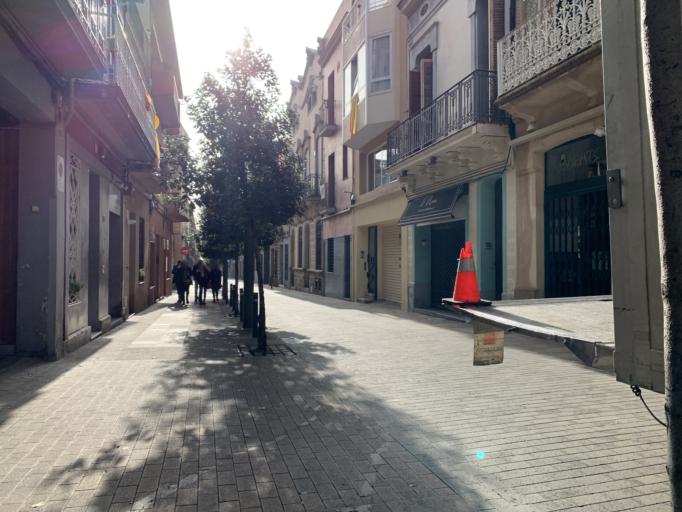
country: ES
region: Catalonia
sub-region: Provincia de Barcelona
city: Mataro
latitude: 41.5367
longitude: 2.4449
